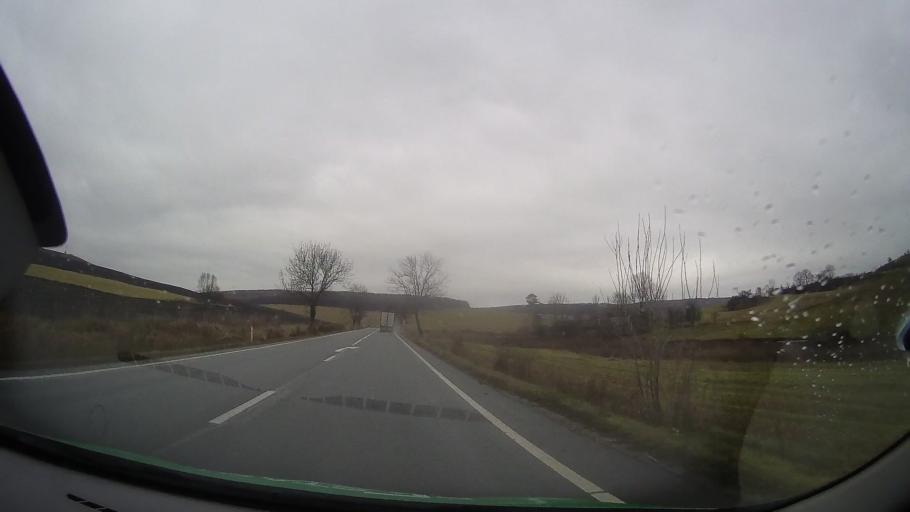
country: RO
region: Mures
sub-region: Comuna Lunca
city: Lunca
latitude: 46.8656
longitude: 24.5539
